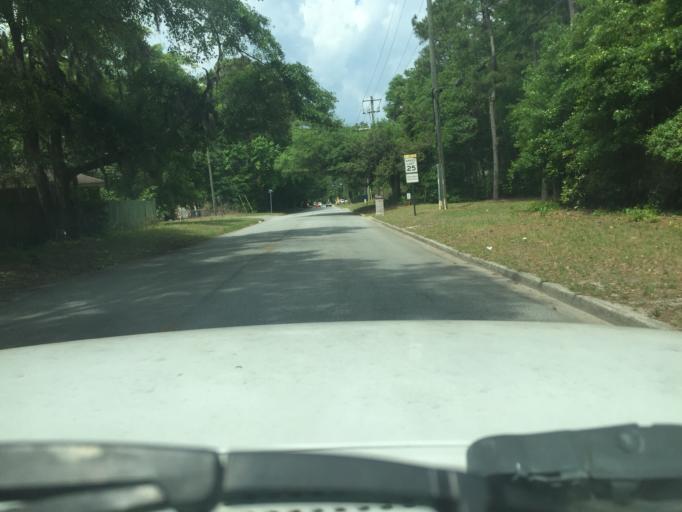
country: US
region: Georgia
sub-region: Chatham County
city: Isle of Hope
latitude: 32.0040
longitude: -81.0718
